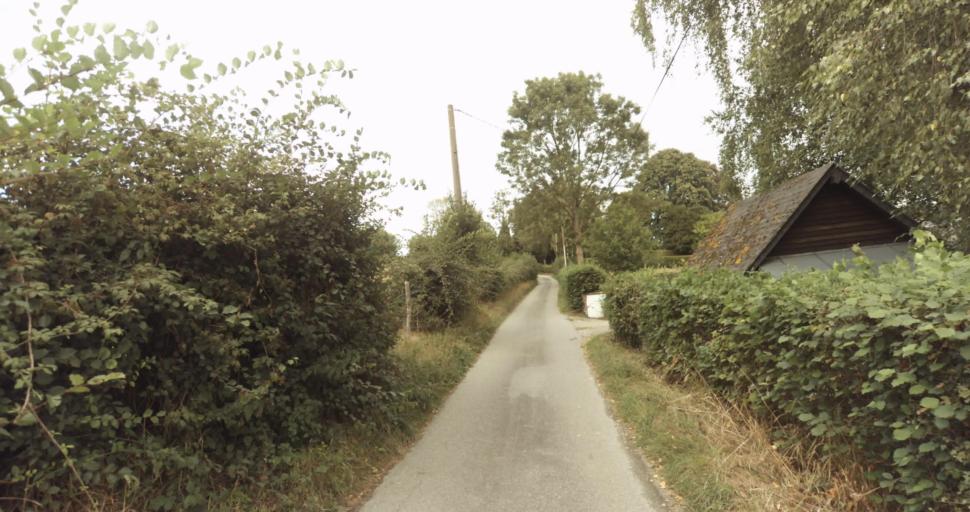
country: FR
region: Lower Normandy
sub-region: Departement de l'Orne
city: Gace
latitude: 48.8481
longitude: 0.2701
